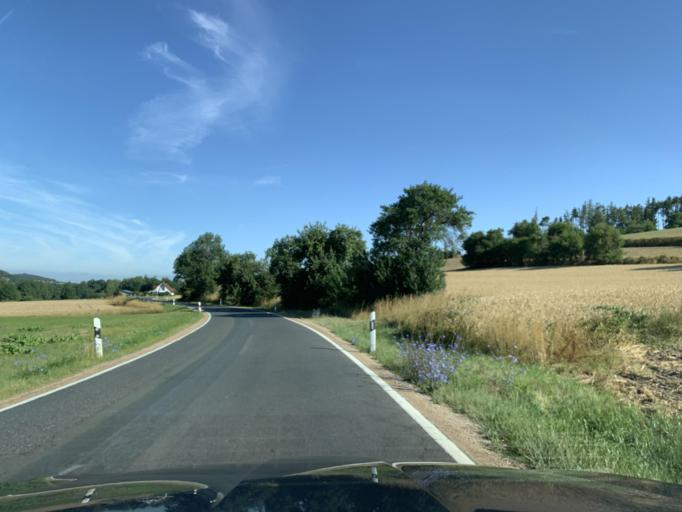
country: DE
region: Bavaria
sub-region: Upper Palatinate
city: Schwarzhofen
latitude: 49.3706
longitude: 12.3504
